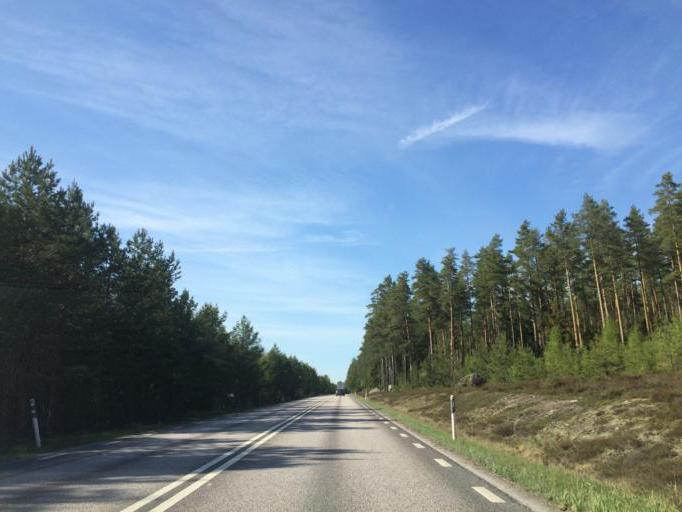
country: SE
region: Soedermanland
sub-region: Katrineholms Kommun
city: Katrineholm
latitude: 59.1194
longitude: 16.1592
